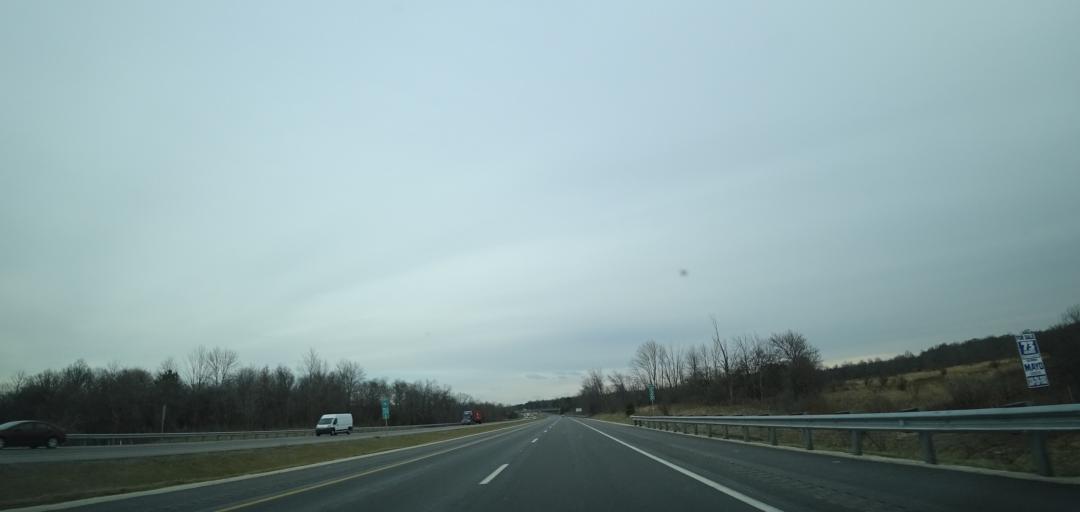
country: US
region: Ohio
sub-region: Mahoning County
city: Austintown
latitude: 41.0982
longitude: -80.8286
